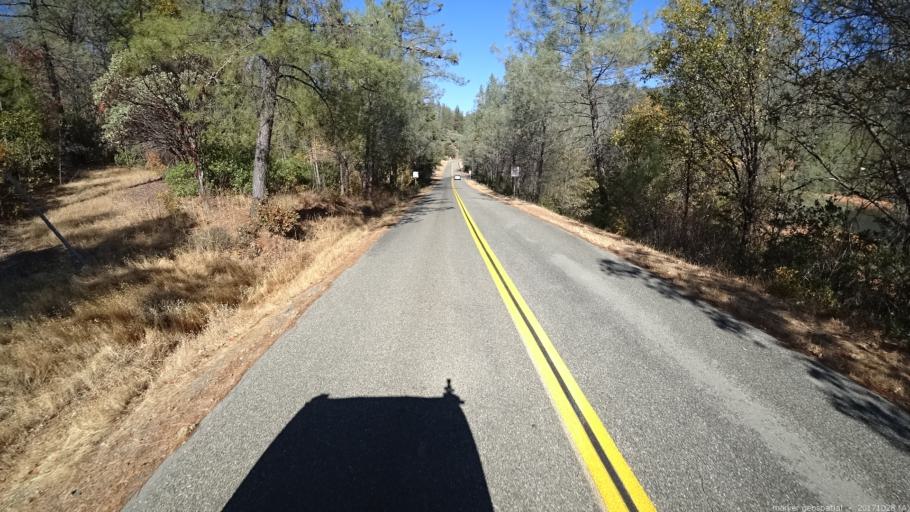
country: US
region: California
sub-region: Shasta County
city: Shasta
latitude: 40.6471
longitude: -122.5579
